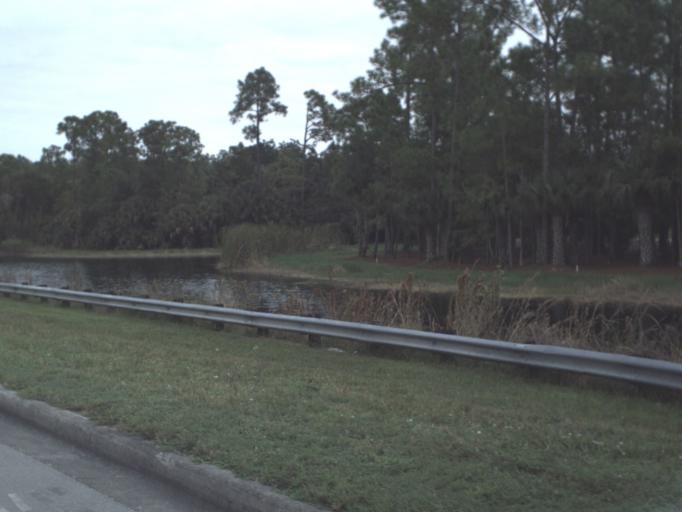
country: US
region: Florida
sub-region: Collier County
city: Golden Gate
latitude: 26.1505
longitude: -81.6865
